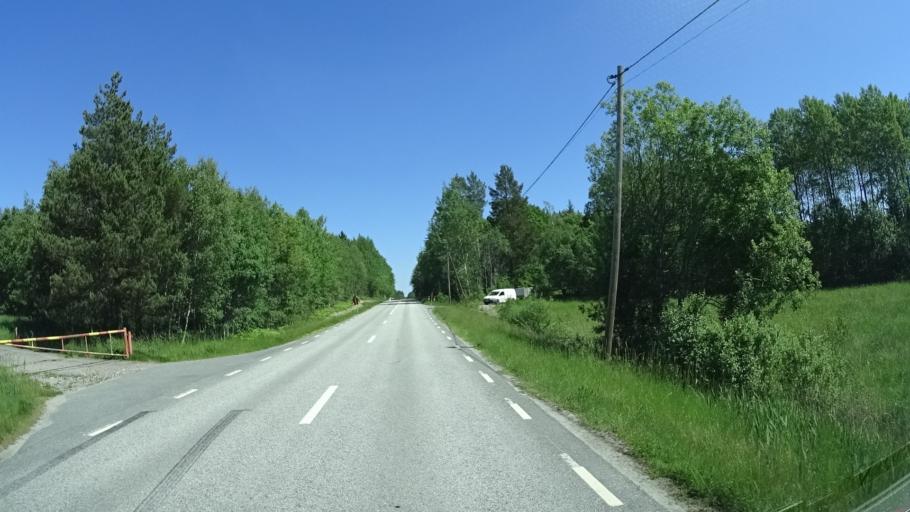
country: SE
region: Stockholm
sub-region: Vallentuna Kommun
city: Vallentuna
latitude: 59.6005
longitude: 18.1266
